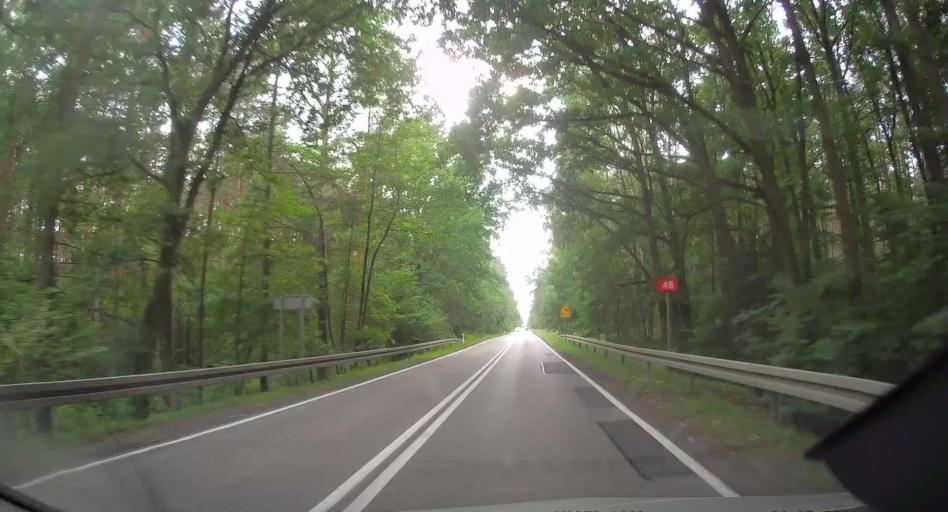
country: PL
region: Lodz Voivodeship
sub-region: Powiat tomaszowski
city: Lubochnia
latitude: 51.5459
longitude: 20.0898
